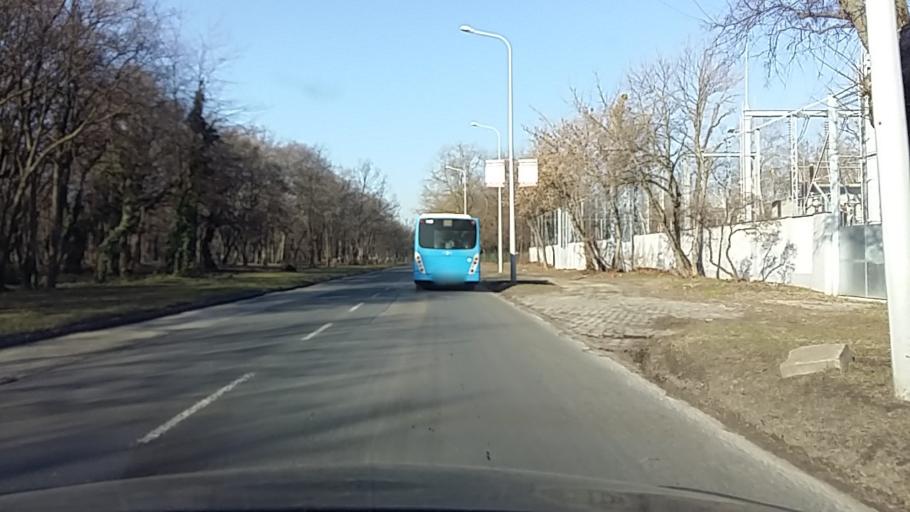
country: HU
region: Budapest
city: Budapest XIV. keruelet
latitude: 47.4795
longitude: 19.1114
